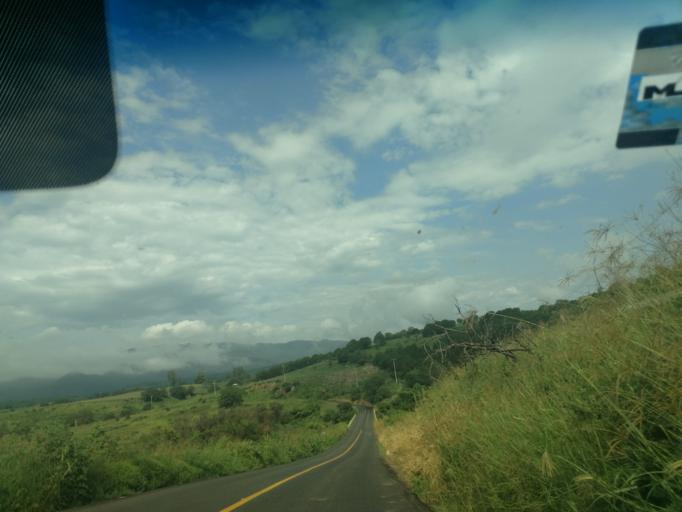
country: MX
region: Jalisco
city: El Salto
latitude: 20.4325
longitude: -104.4827
